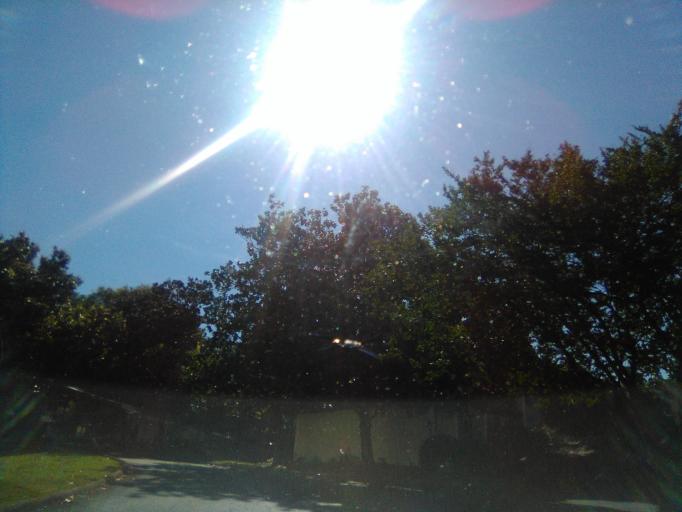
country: US
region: Tennessee
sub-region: Davidson County
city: Belle Meade
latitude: 36.1227
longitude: -86.8477
